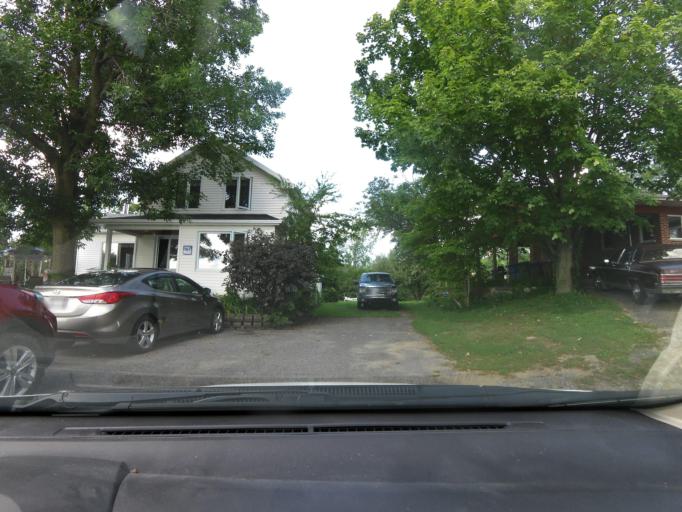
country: CA
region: Quebec
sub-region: Capitale-Nationale
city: Saint-Marc-des-Carrieres
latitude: 46.5875
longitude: -72.0394
